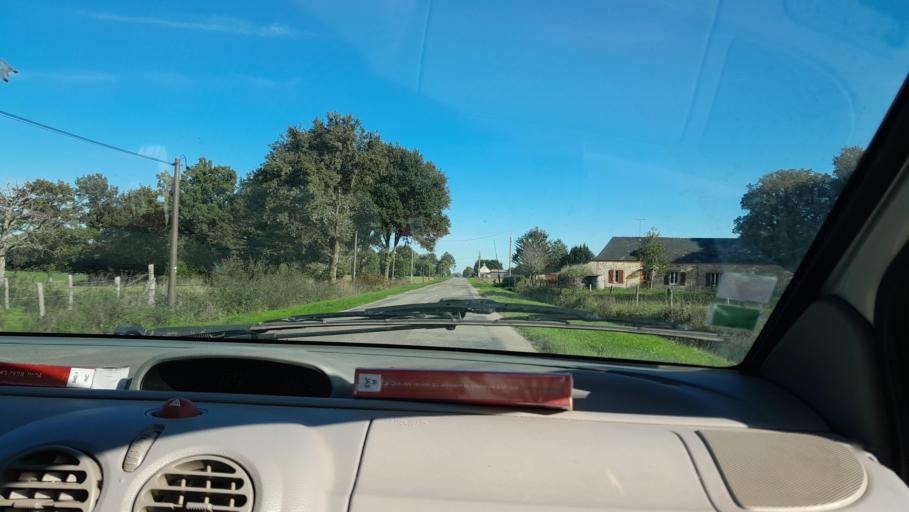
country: FR
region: Brittany
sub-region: Departement d'Ille-et-Vilaine
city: Le Pertre
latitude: 47.9691
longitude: -1.0943
